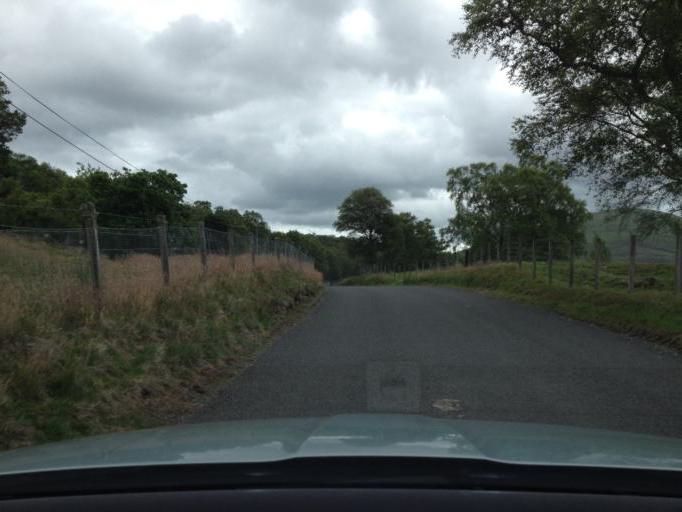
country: GB
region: Scotland
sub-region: Aberdeenshire
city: Aboyne
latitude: 56.8961
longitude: -2.7982
